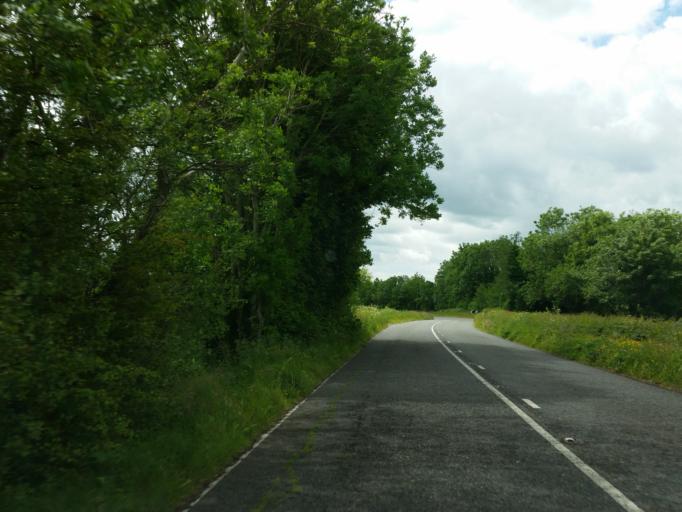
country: GB
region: Northern Ireland
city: Fivemiletown
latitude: 54.4452
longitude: -7.0868
